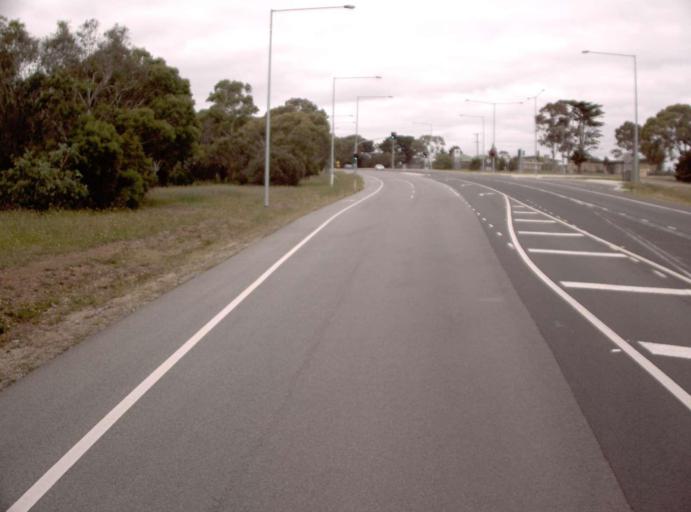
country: AU
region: Victoria
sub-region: Mornington Peninsula
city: Mount Martha
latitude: -38.2720
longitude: 145.0340
